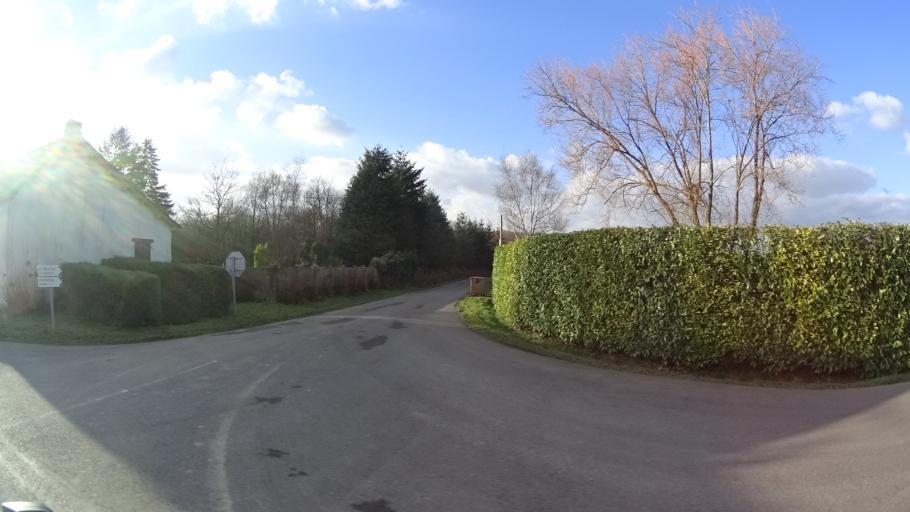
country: FR
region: Pays de la Loire
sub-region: Departement de la Loire-Atlantique
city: Guemene-Penfao
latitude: 47.6028
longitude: -1.8451
